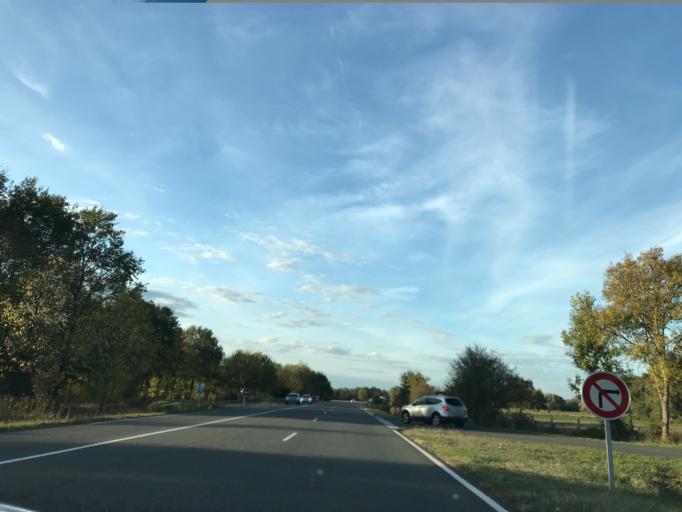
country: FR
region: Auvergne
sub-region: Departement de l'Allier
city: Saint-Yorre
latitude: 46.0208
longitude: 3.4809
